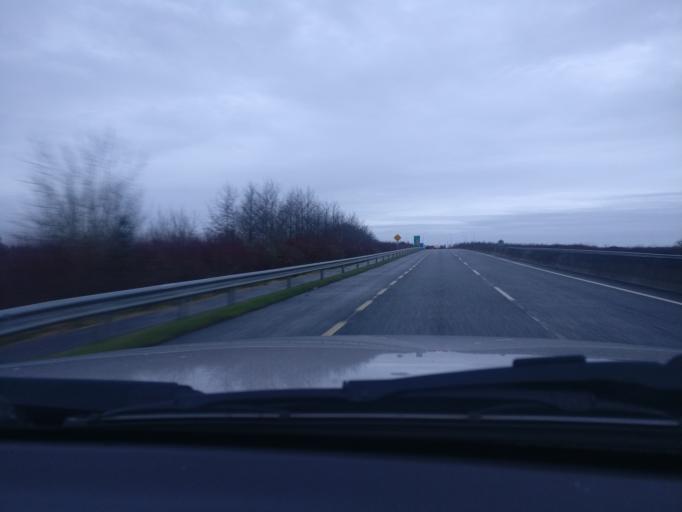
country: IE
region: Leinster
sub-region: An Mhi
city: Navan
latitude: 53.6420
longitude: -6.7347
